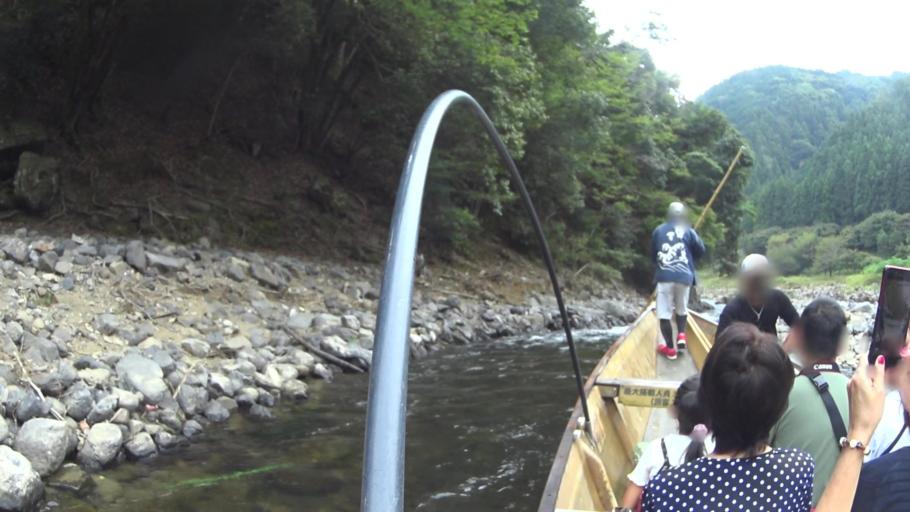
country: JP
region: Kyoto
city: Kameoka
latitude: 35.0185
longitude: 135.6317
